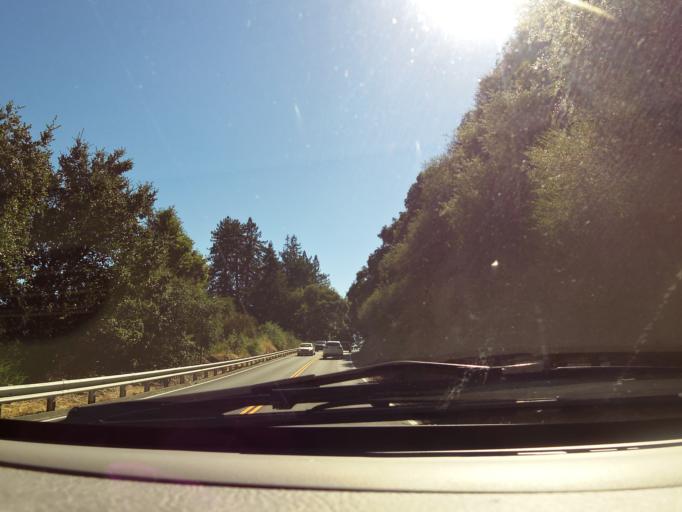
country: US
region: California
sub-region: Santa Cruz County
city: Interlaken
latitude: 36.9907
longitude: -121.7141
